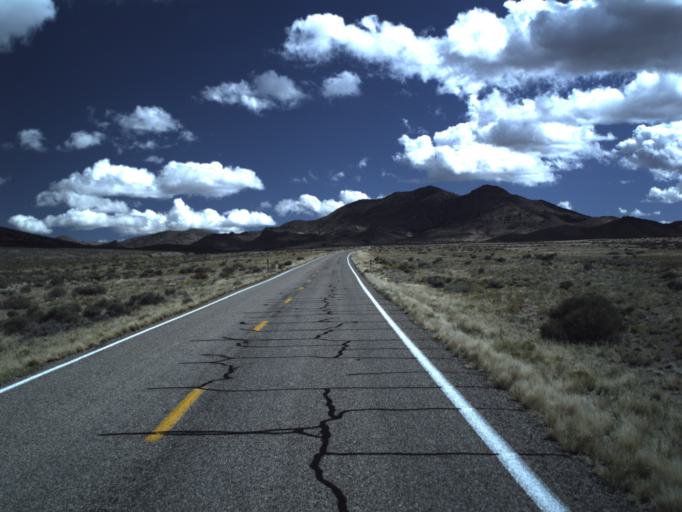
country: US
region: Utah
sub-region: Beaver County
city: Milford
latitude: 38.4440
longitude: -113.3260
